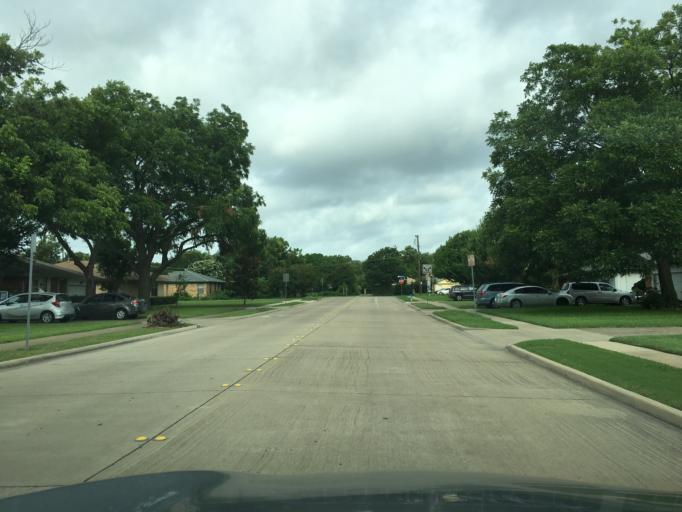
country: US
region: Texas
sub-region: Dallas County
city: Richardson
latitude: 32.9453
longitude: -96.7271
